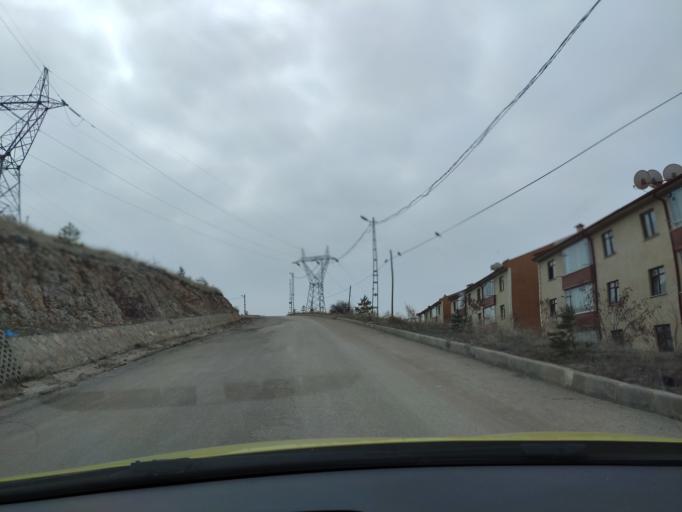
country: TR
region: Bayburt
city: Bayburt
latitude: 40.2616
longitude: 40.2163
